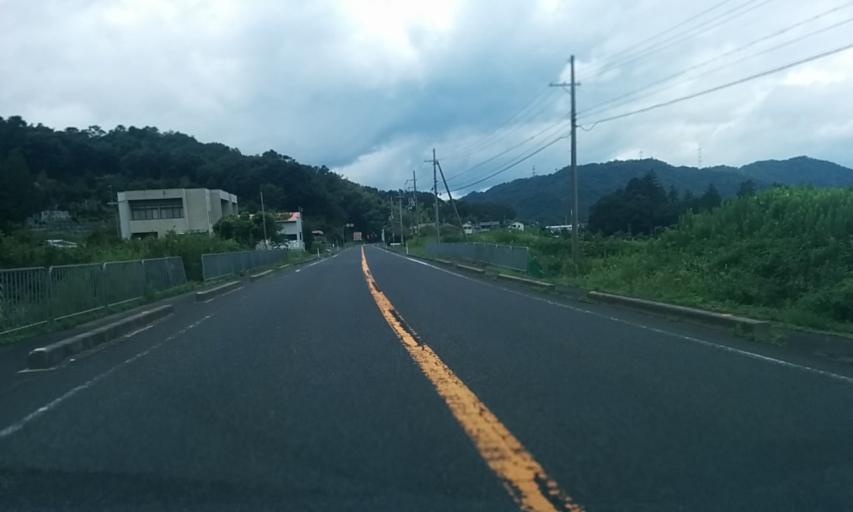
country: JP
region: Kyoto
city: Miyazu
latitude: 35.5420
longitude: 135.2346
